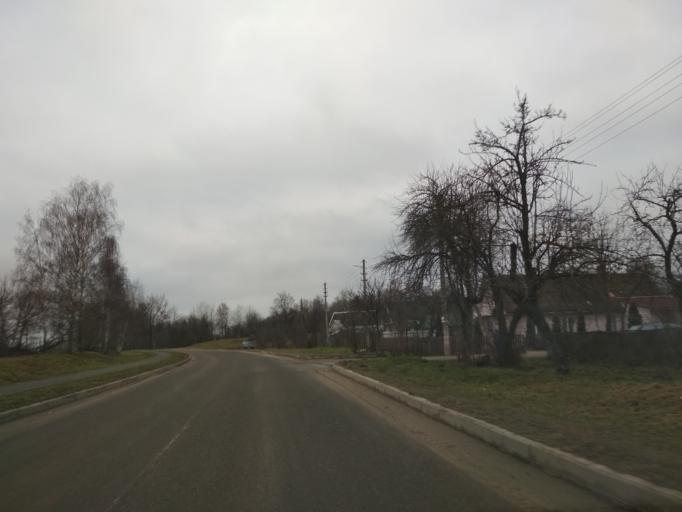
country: BY
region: Minsk
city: Mar''ina Horka
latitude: 53.5274
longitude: 28.1325
